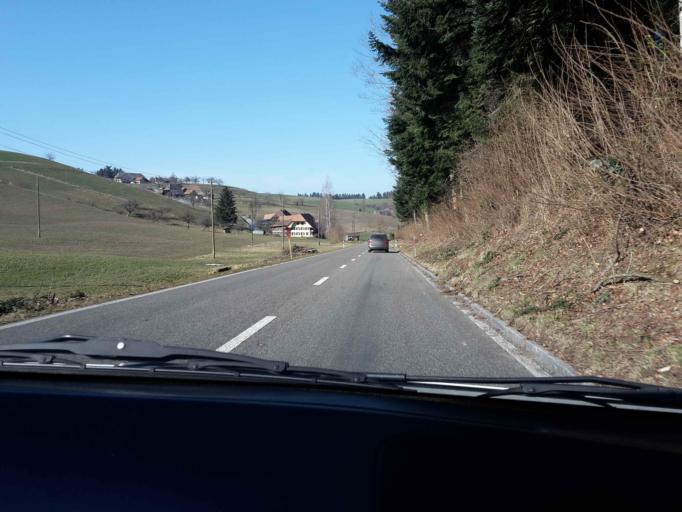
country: CH
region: Bern
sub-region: Emmental District
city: Durrenroth
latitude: 47.1048
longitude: 7.7762
